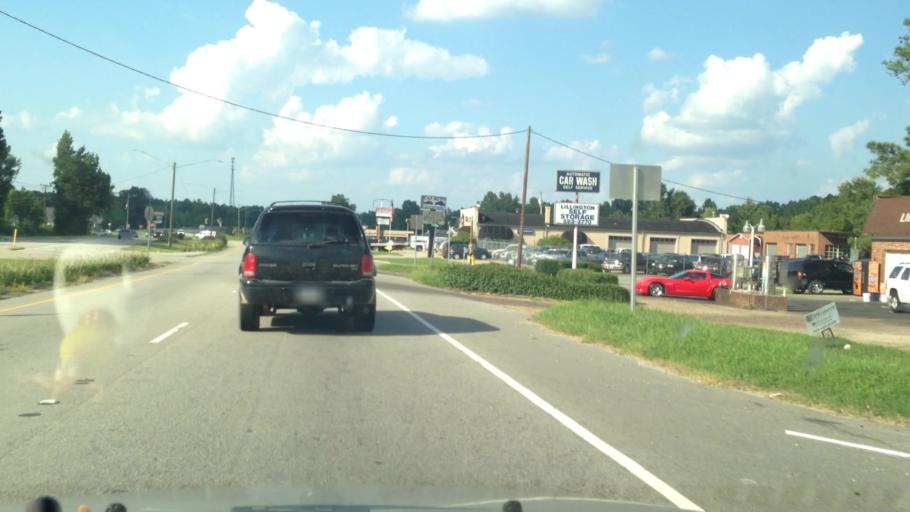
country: US
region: North Carolina
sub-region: Harnett County
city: Lillington
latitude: 35.4018
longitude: -78.8149
